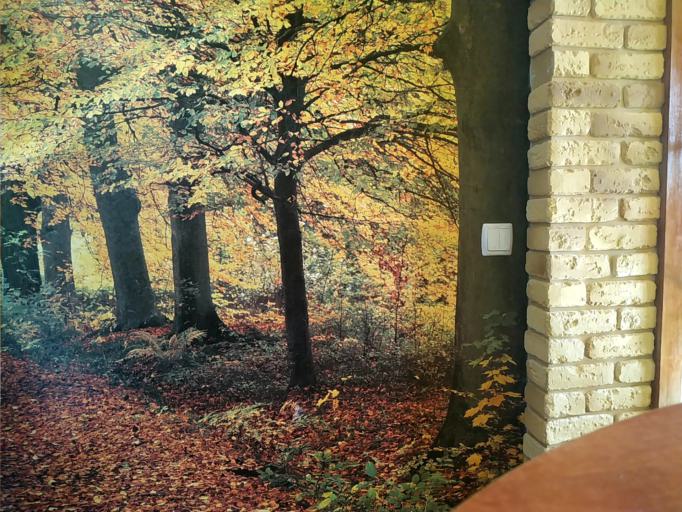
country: RU
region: Jaroslavl
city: Kukoboy
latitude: 58.8378
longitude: 39.7491
